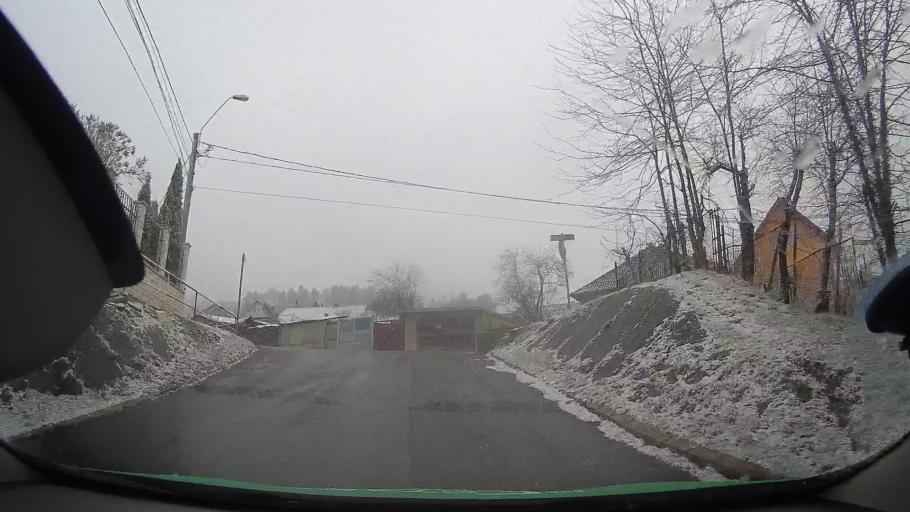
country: RO
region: Sibiu
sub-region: Municipiul Medias
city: Medias
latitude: 46.1617
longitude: 24.3644
